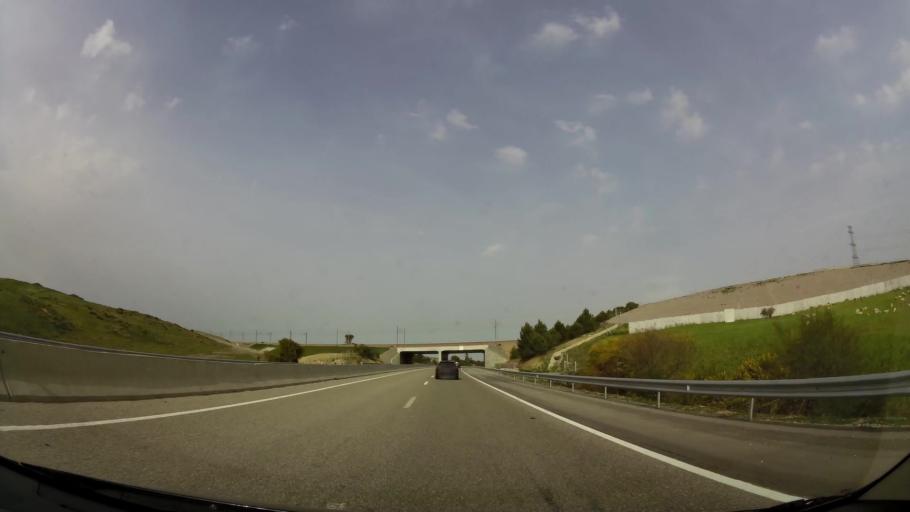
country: MA
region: Tanger-Tetouan
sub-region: Tanger-Assilah
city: Tangier
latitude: 35.6774
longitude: -5.8076
